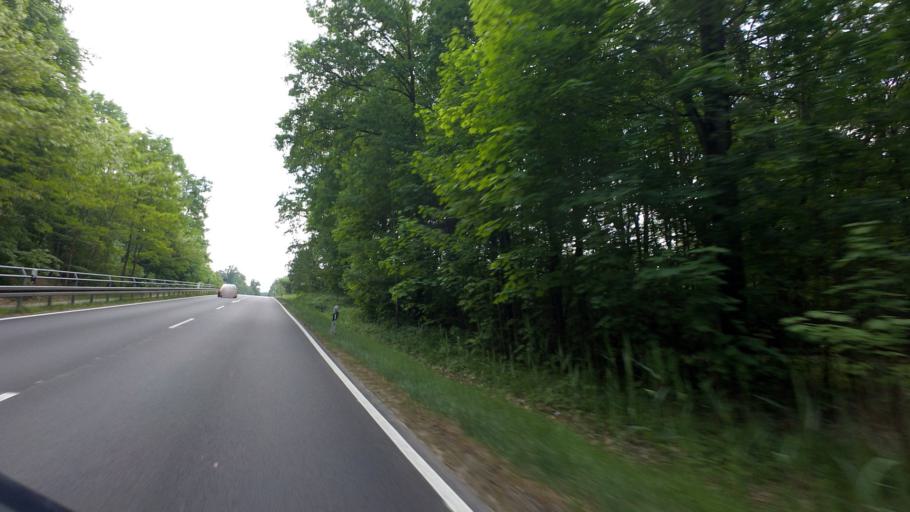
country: DE
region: Saxony
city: Rietschen
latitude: 51.3853
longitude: 14.7867
